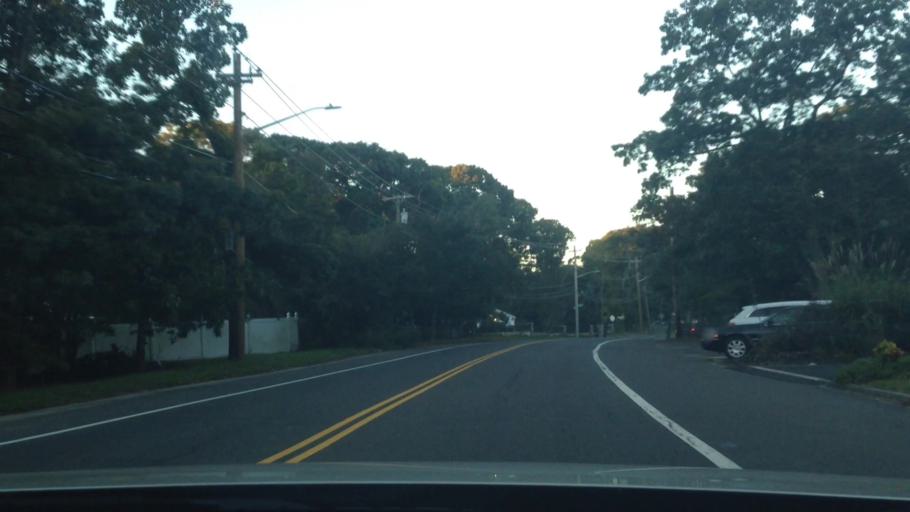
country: US
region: New York
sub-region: Suffolk County
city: Selden
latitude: 40.8568
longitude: -73.0299
